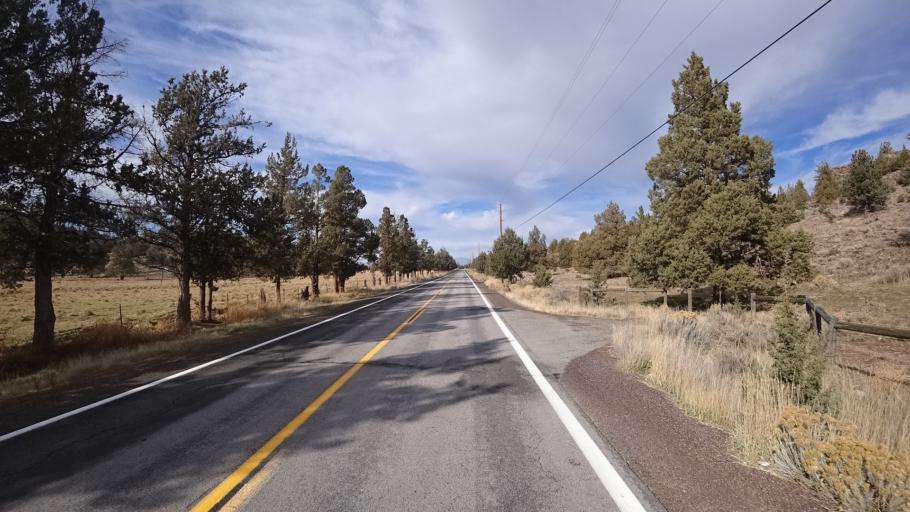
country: US
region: California
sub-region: Siskiyou County
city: Weed
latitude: 41.5758
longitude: -122.3949
